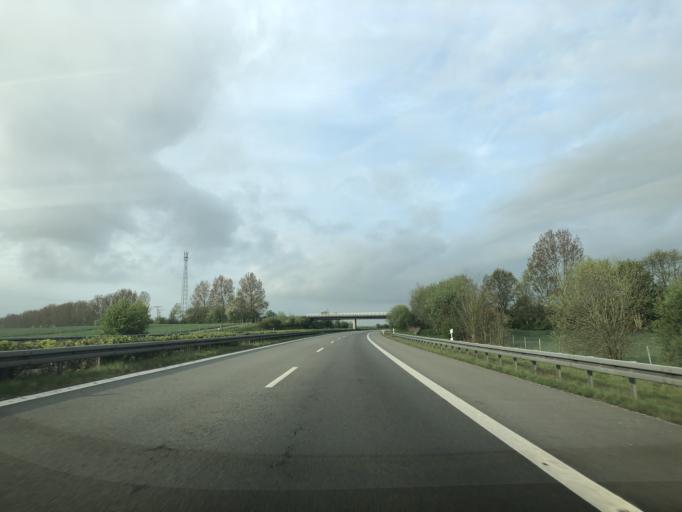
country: DE
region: Mecklenburg-Vorpommern
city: Bad Sulze
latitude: 54.0302
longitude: 12.5970
